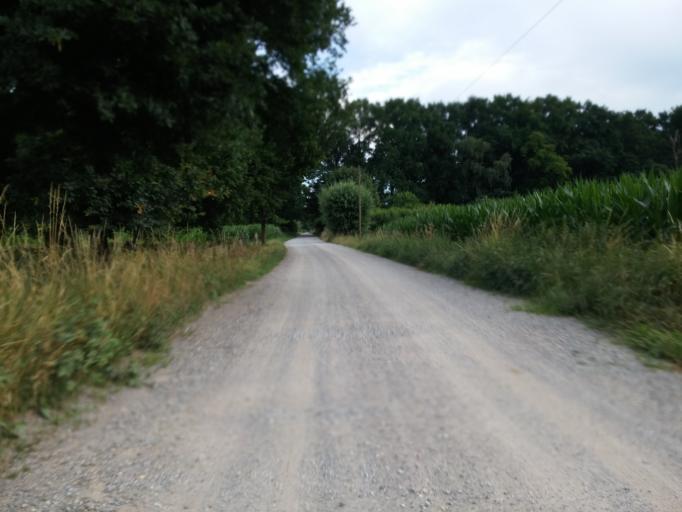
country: DE
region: North Rhine-Westphalia
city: Tonisvorst
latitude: 51.3881
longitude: 6.5239
